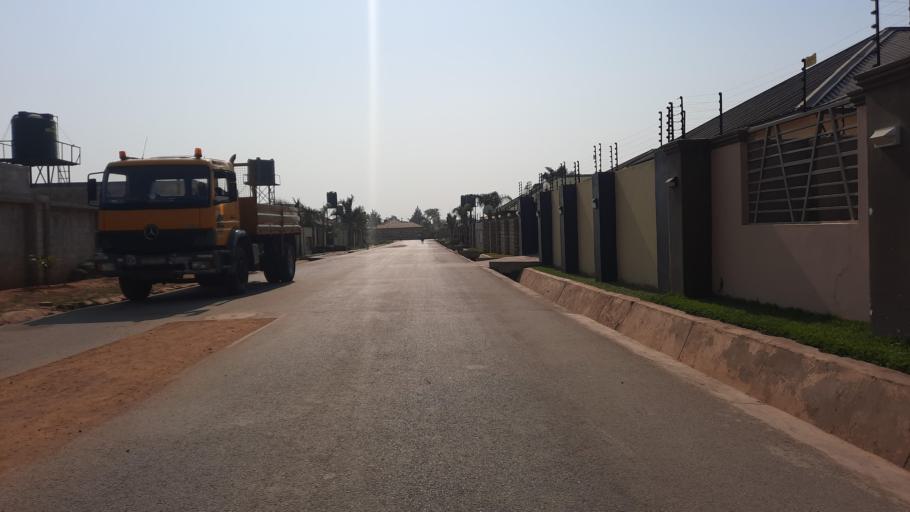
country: ZM
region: Lusaka
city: Lusaka
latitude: -15.3922
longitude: 28.3882
